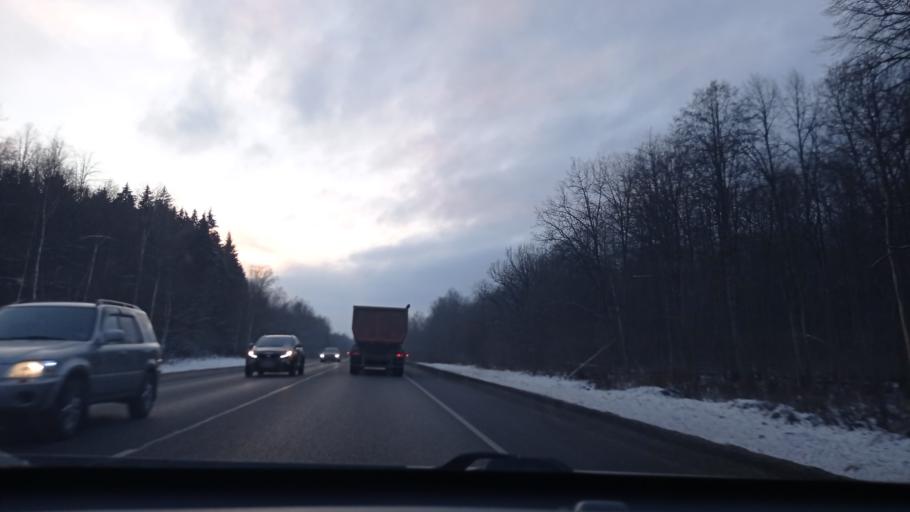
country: RU
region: Kaluga
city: Zhukovo
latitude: 55.1717
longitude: 36.8688
